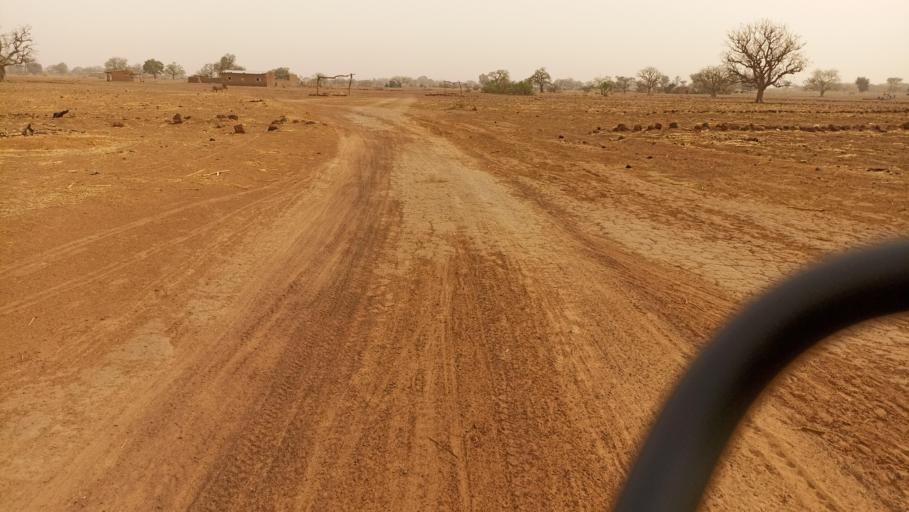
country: BF
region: Nord
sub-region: Province du Zondoma
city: Gourcy
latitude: 13.1411
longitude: -2.5975
